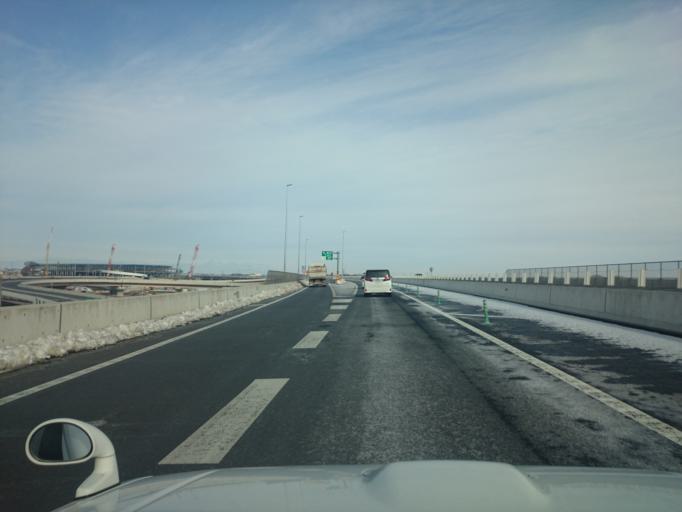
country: JP
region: Ibaraki
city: Sakai
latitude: 36.0927
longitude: 139.7619
